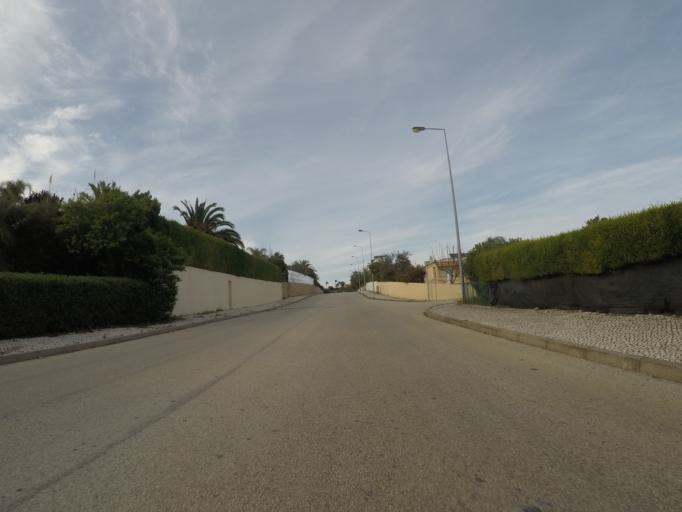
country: PT
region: Faro
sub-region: Lagos
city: Lagos
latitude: 37.0892
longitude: -8.7365
